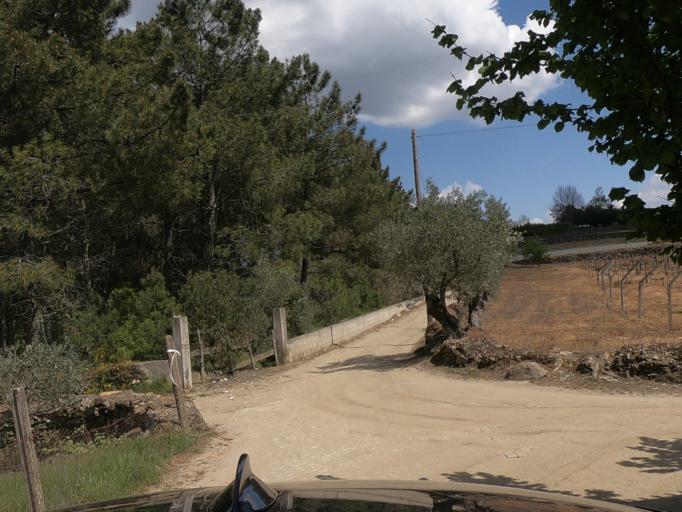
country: PT
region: Vila Real
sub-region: Sabrosa
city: Vilela
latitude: 41.2241
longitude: -7.6813
